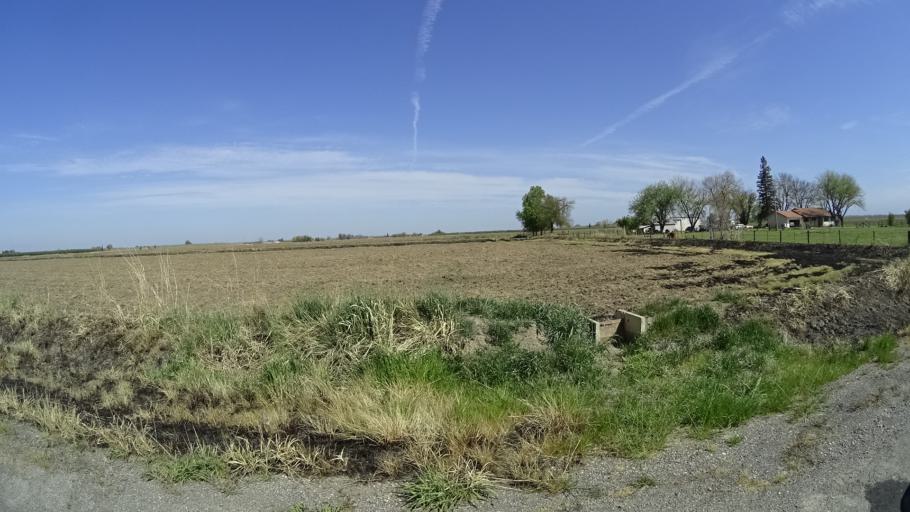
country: US
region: California
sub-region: Glenn County
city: Hamilton City
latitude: 39.6088
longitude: -122.0327
